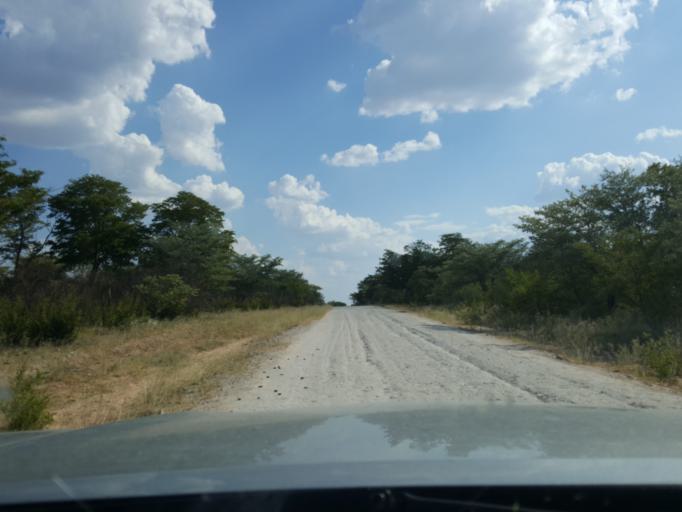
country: BW
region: North West
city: Shakawe
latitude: -18.7796
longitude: 21.7704
